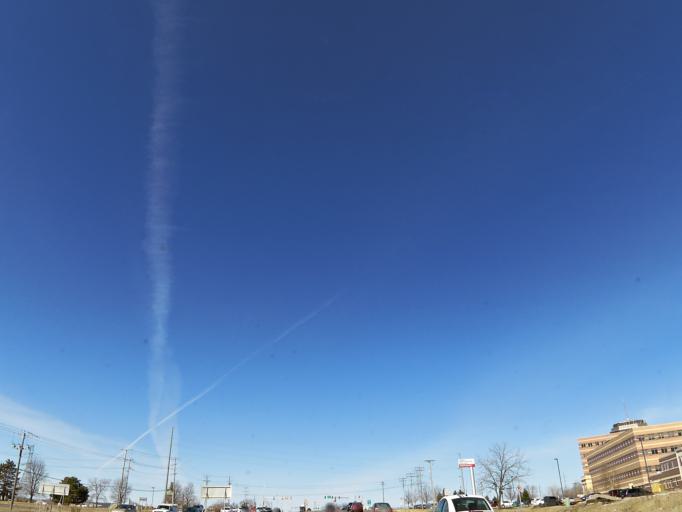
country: US
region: Minnesota
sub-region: Hennepin County
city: Plymouth
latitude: 45.0093
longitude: -93.4528
